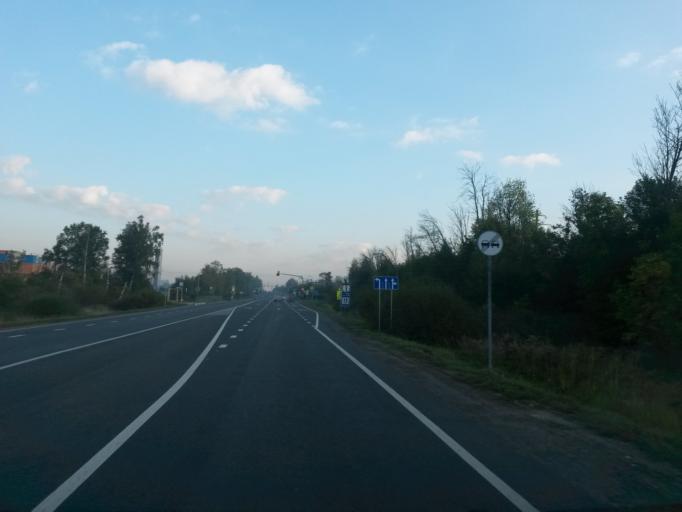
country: RU
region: Moskovskaya
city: Vostryakovo
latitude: 55.3677
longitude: 37.7876
